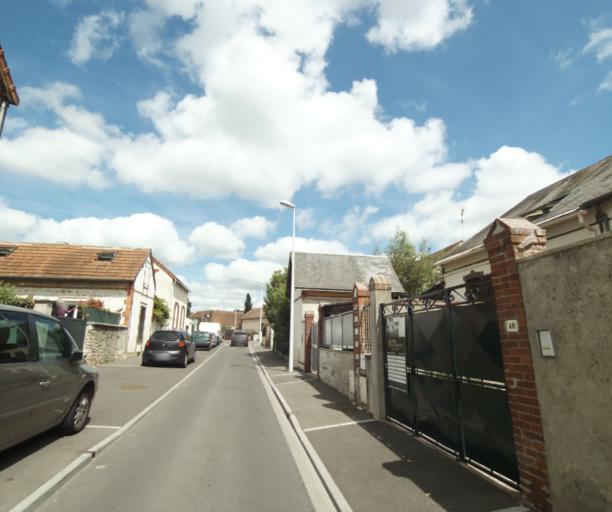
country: FR
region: Centre
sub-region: Departement d'Eure-et-Loir
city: Luisant
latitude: 48.4383
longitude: 1.4772
